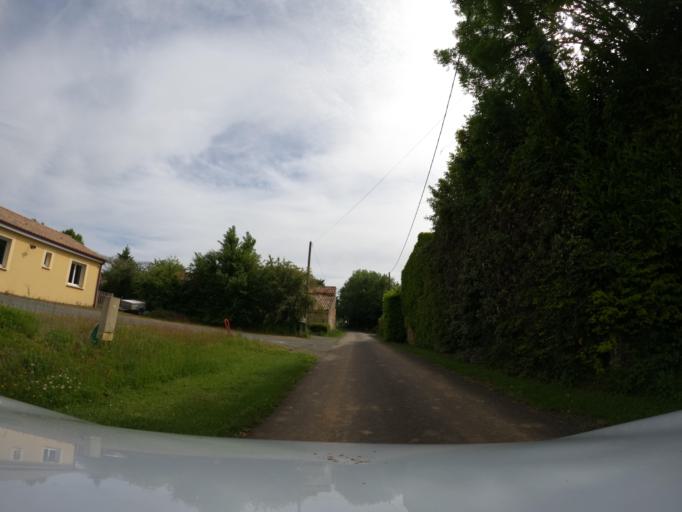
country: FR
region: Pays de la Loire
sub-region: Departement de la Vendee
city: Saint-Hilaire-des-Loges
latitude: 46.4965
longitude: -0.6514
